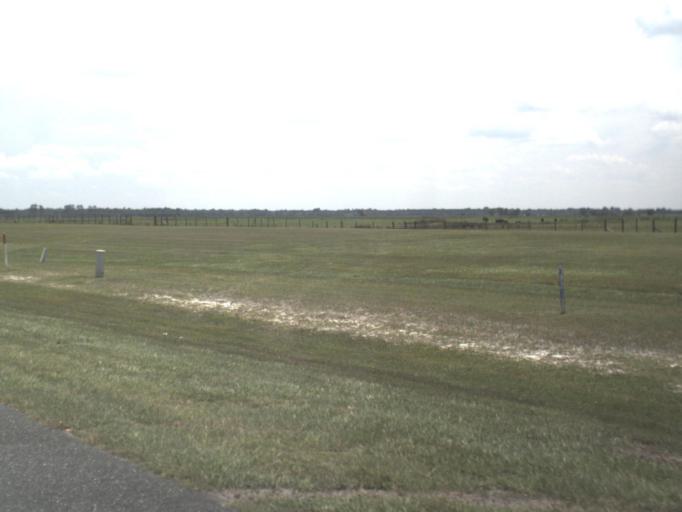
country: US
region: Florida
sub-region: Bradford County
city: Starke
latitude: 30.0595
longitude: -82.1791
